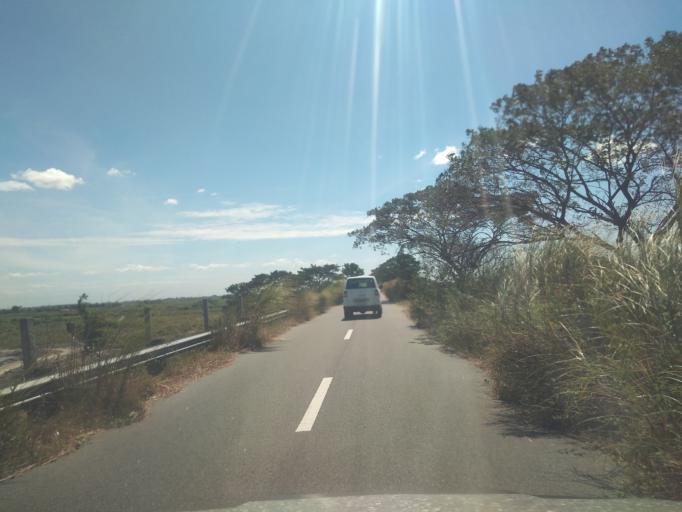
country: PH
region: Central Luzon
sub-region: Province of Pampanga
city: San Basilio
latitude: 15.0370
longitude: 120.5958
